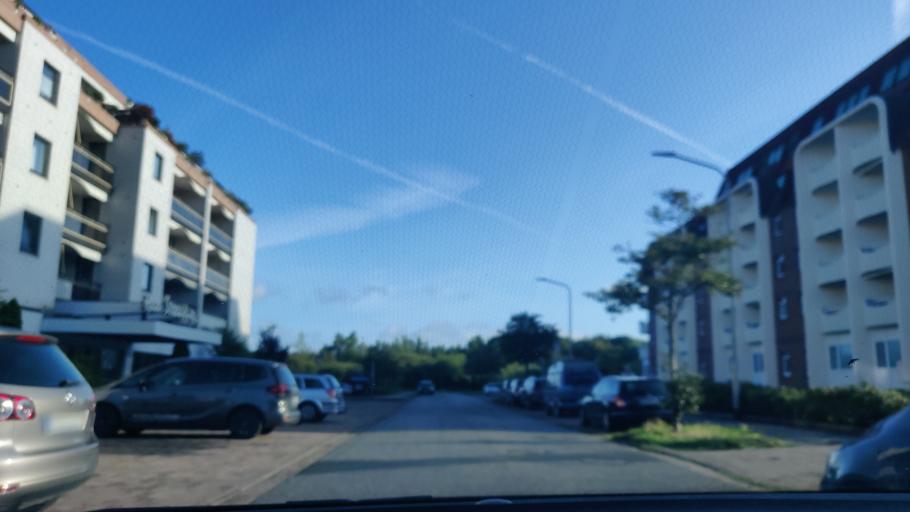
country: DE
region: Lower Saxony
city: Cuxhaven
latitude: 53.8881
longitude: 8.6706
